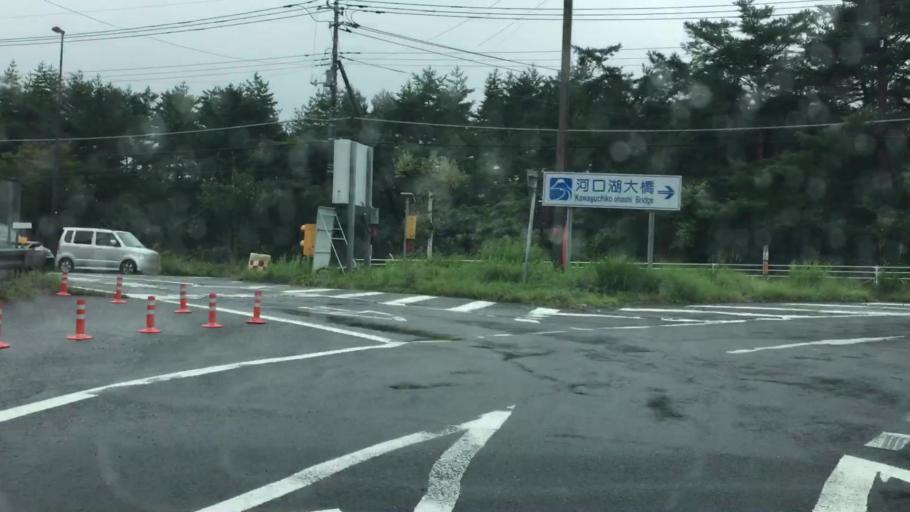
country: JP
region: Yamanashi
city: Fujikawaguchiko
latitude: 35.4849
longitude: 138.7749
